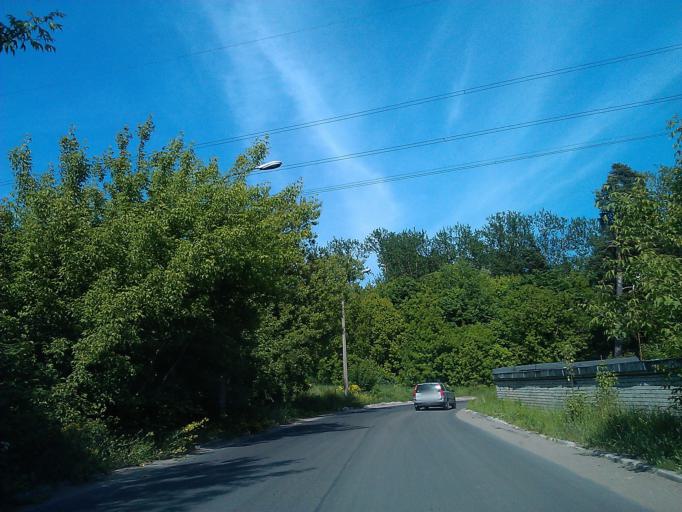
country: LV
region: Riga
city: Jaunciems
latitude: 56.9882
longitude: 24.2030
